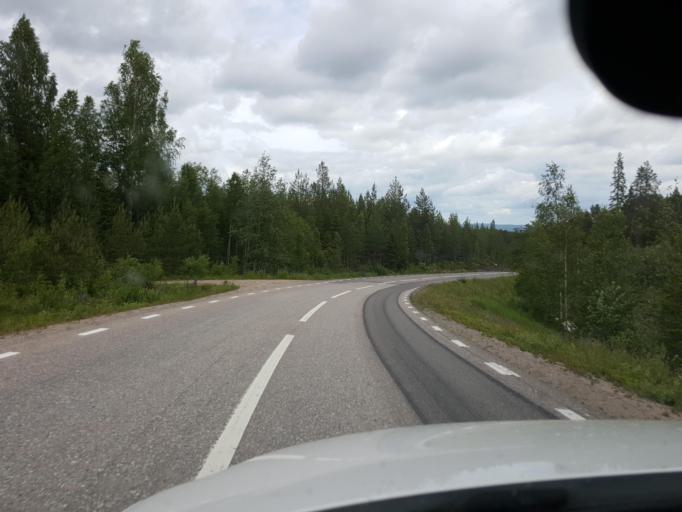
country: SE
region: Gaevleborg
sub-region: Ljusdals Kommun
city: Farila
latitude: 61.7754
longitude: 15.5884
